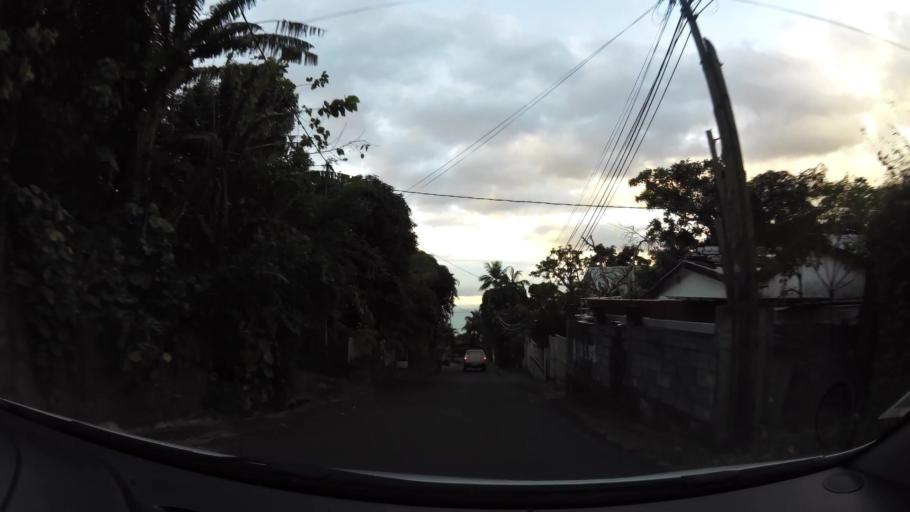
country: RE
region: Reunion
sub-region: Reunion
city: Saint-Denis
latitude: -20.9133
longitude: 55.4593
